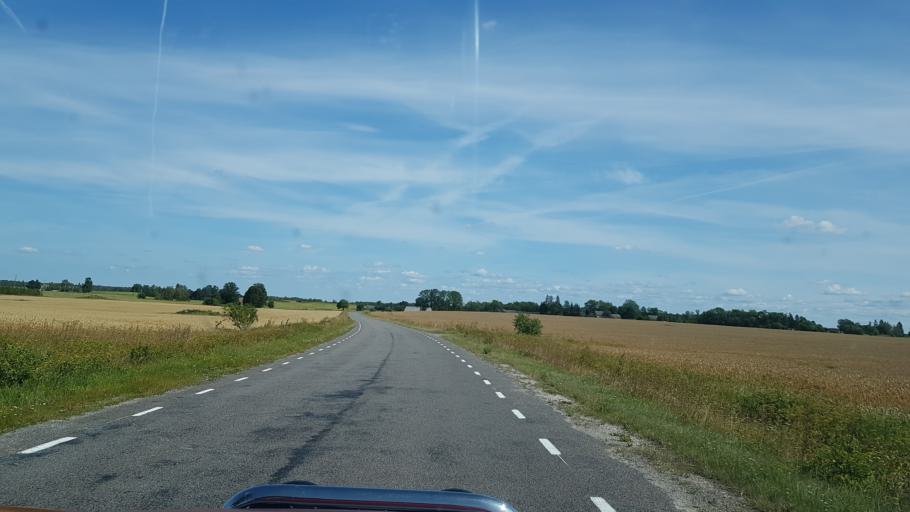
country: EE
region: Jaervamaa
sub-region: Koeru vald
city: Koeru
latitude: 59.0406
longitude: 25.9998
